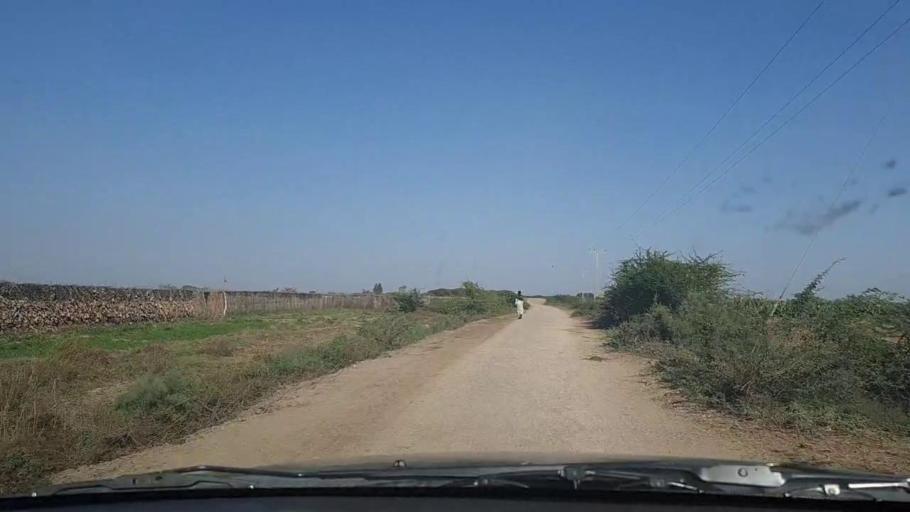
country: PK
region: Sindh
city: Chuhar Jamali
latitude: 24.3244
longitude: 67.7526
